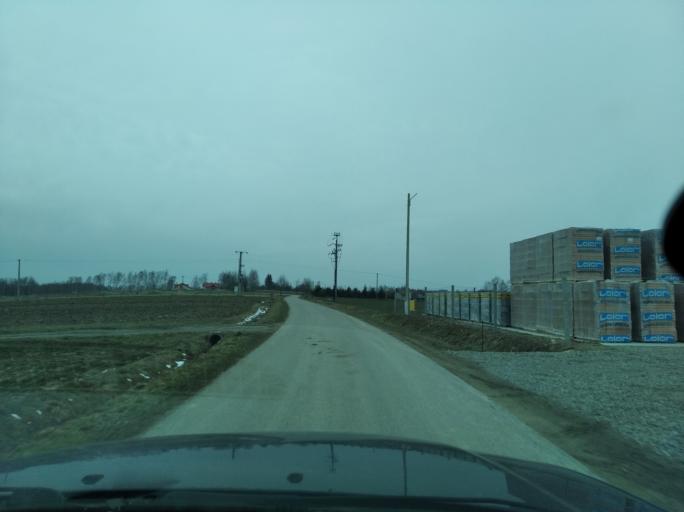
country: PL
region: Subcarpathian Voivodeship
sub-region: Powiat rzeszowski
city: Chmielnik
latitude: 49.9869
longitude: 22.1516
